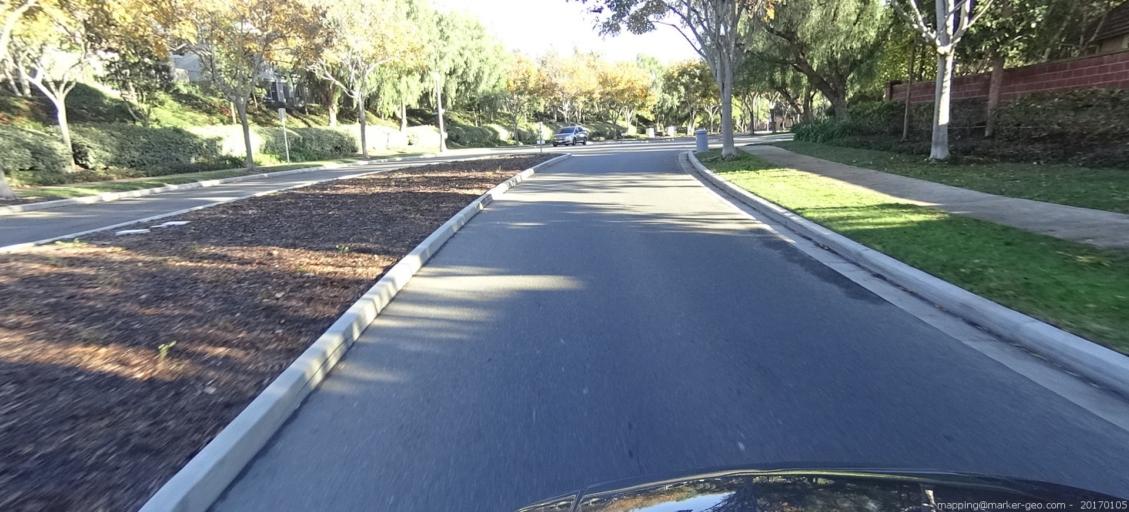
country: US
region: California
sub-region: Orange County
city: Ladera Ranch
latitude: 33.5544
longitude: -117.6418
